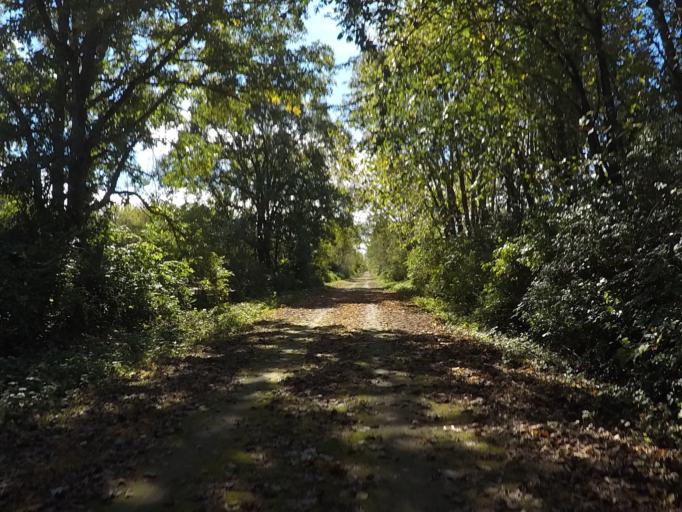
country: US
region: Wisconsin
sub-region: Richland County
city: Richland Center
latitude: 43.2811
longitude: -90.3173
